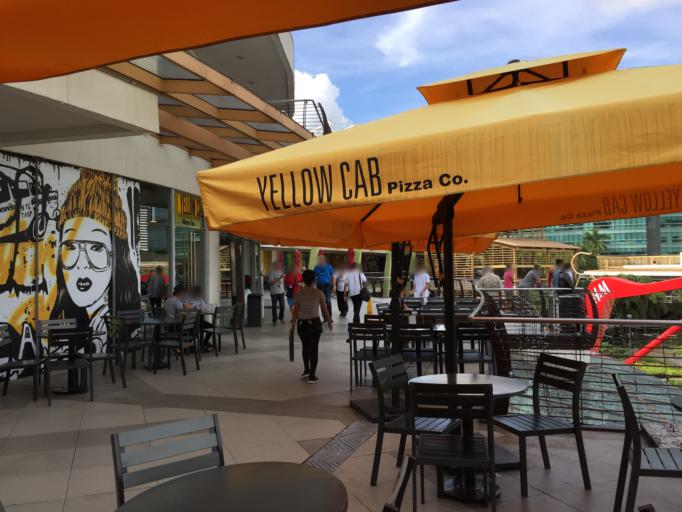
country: PH
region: Central Visayas
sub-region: Cebu City
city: Baugo
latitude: 10.3183
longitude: 123.9055
